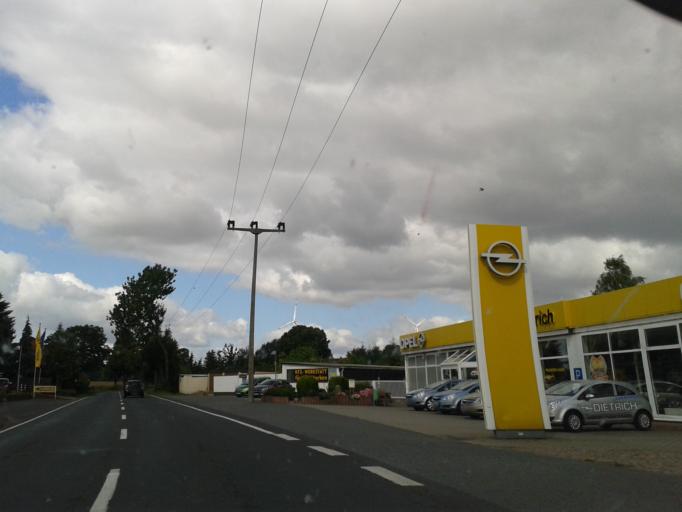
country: DE
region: Saxony-Anhalt
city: Beesenstedt
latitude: 51.5607
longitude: 11.7124
